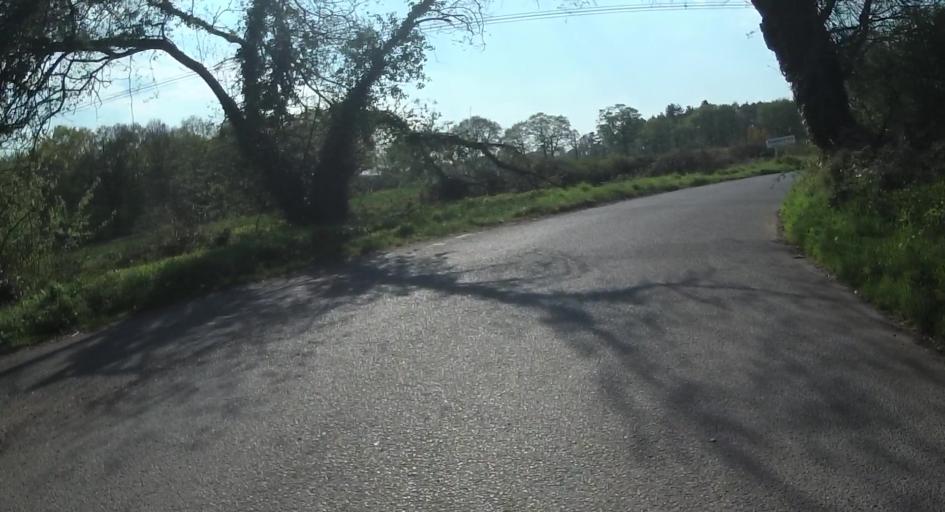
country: GB
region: England
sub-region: West Berkshire
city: Stratfield Mortimer
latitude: 51.3554
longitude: -1.0665
